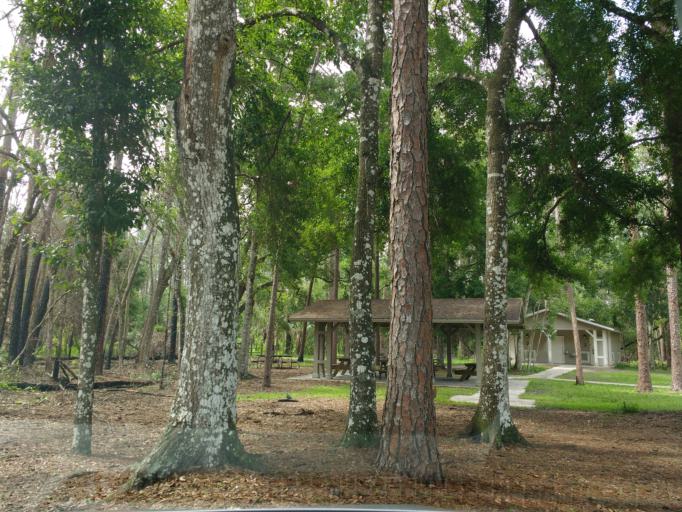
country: US
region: Florida
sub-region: Highlands County
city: Sebring
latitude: 27.4699
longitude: -81.5324
